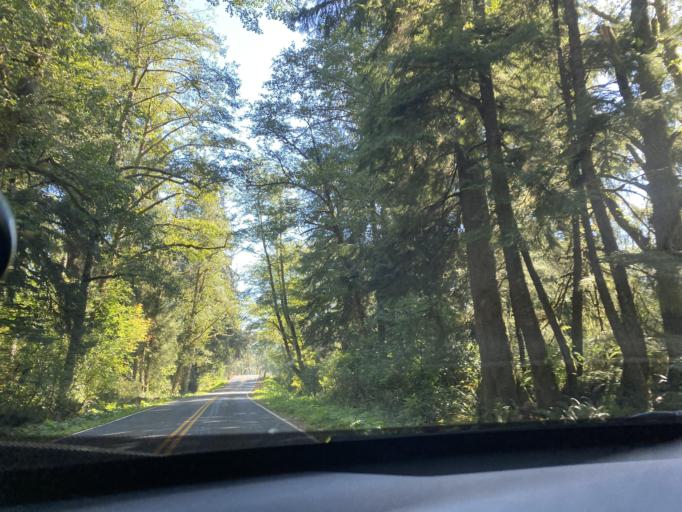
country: US
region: Washington
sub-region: Clallam County
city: Forks
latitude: 47.9224
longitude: -124.6221
